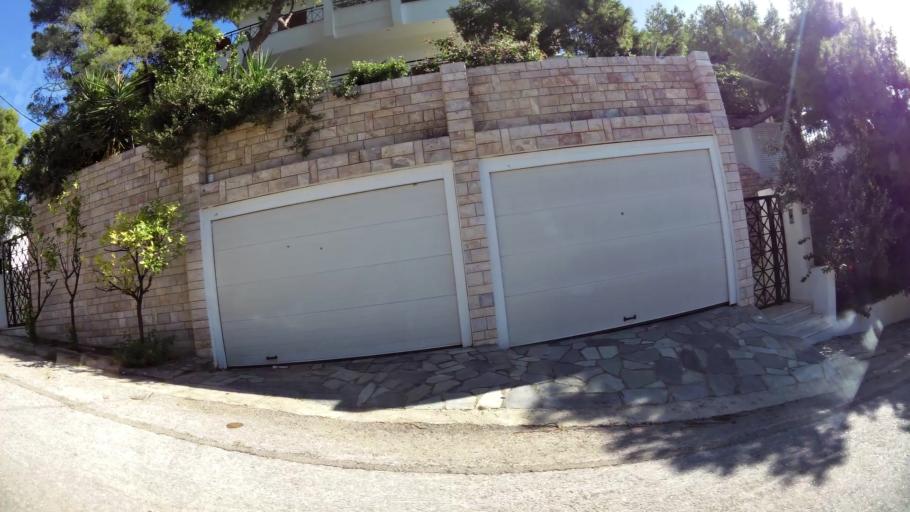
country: GR
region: Attica
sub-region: Nomarchia Anatolikis Attikis
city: Vouliagmeni
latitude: 37.8198
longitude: 23.7785
